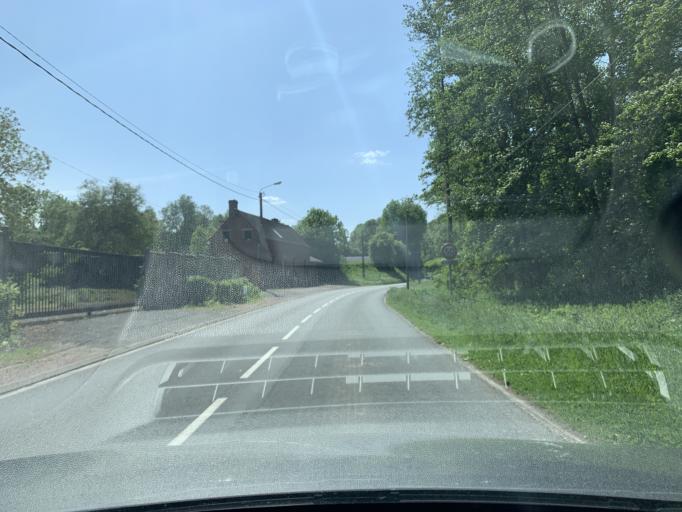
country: FR
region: Nord-Pas-de-Calais
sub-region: Departement du Nord
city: Marcoing
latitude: 50.1266
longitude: 3.1890
